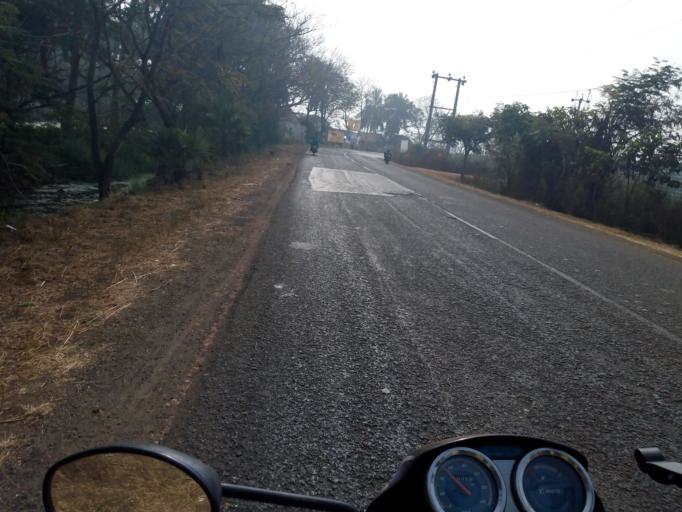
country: IN
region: Andhra Pradesh
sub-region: West Godavari
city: Tadepallegudem
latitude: 16.7921
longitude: 81.4183
